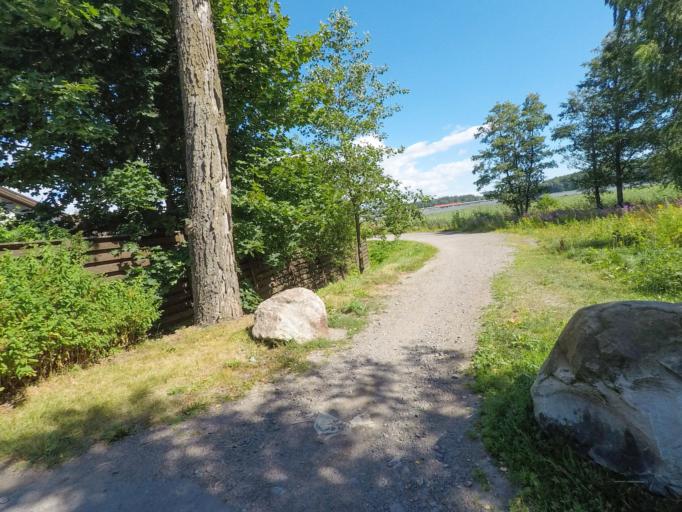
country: FI
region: Uusimaa
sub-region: Helsinki
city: Vantaa
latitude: 60.2028
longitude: 25.0962
